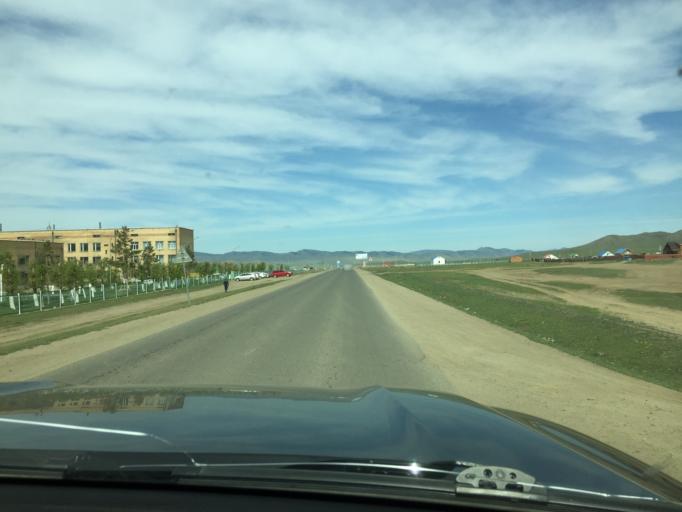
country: MN
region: Central Aimak
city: Ihsueuej
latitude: 48.2260
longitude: 106.2905
